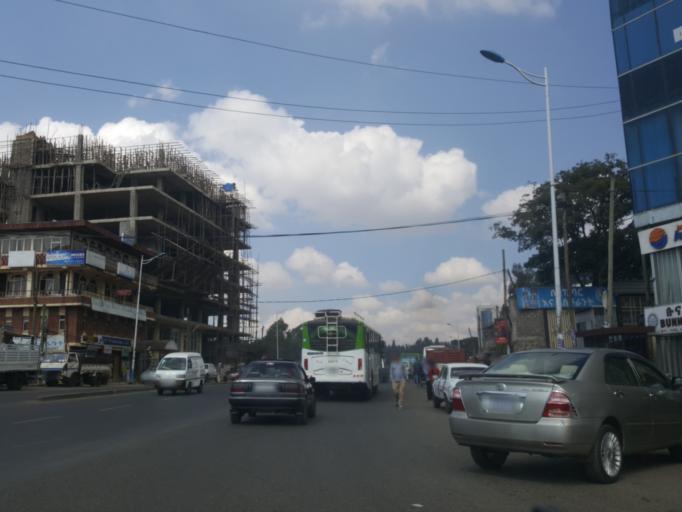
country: ET
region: Adis Abeba
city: Addis Ababa
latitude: 9.0531
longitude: 38.7199
